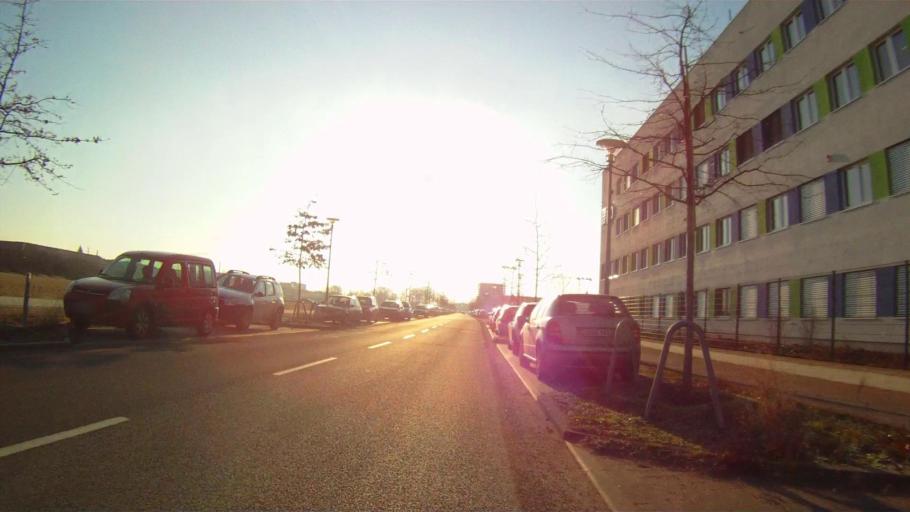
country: DE
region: Berlin
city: Adlershof
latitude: 52.4372
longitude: 13.5344
